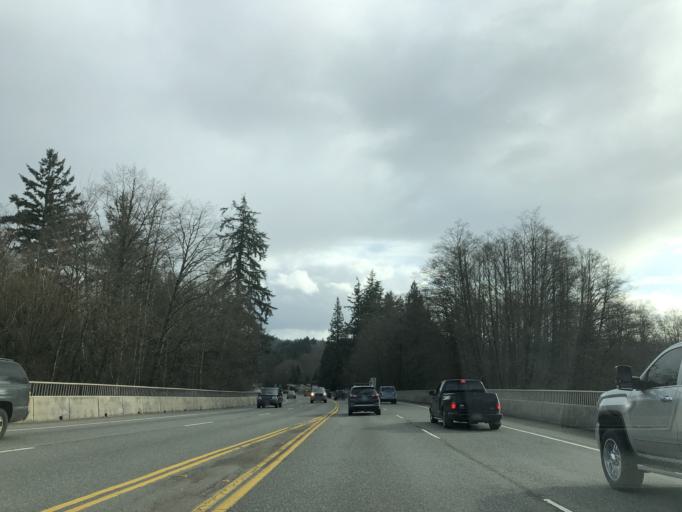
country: US
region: Washington
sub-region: Kitsap County
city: Poulsbo
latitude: 47.7565
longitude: -122.6513
